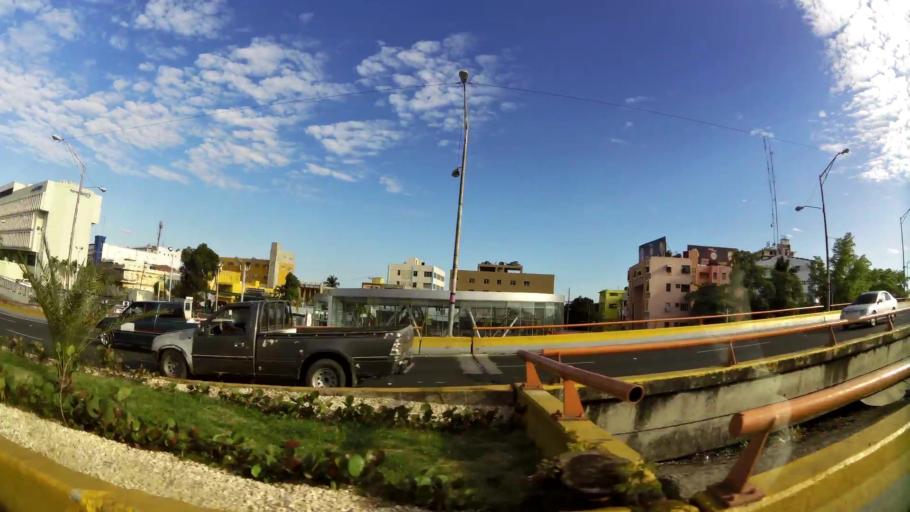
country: DO
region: Nacional
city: San Carlos
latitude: 18.4815
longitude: -69.9068
